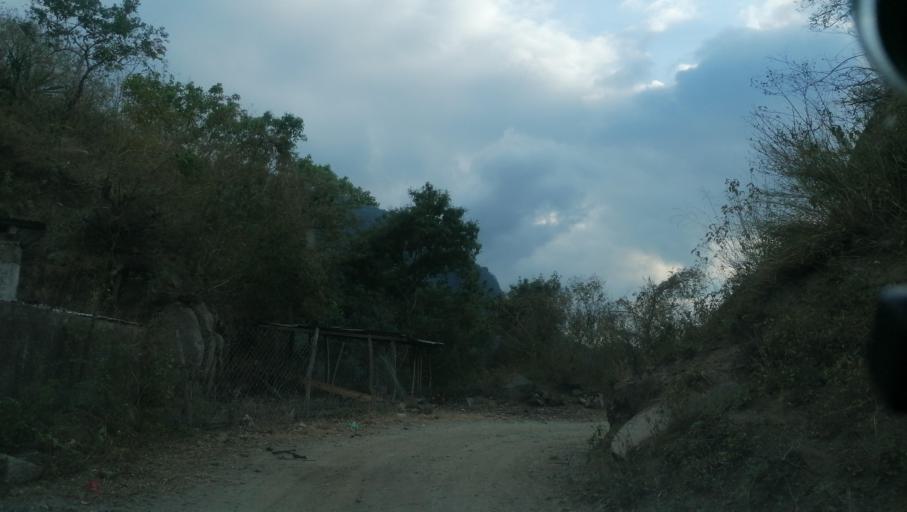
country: MX
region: Chiapas
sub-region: Cacahoatan
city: Benito Juarez
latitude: 15.1454
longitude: -92.1859
